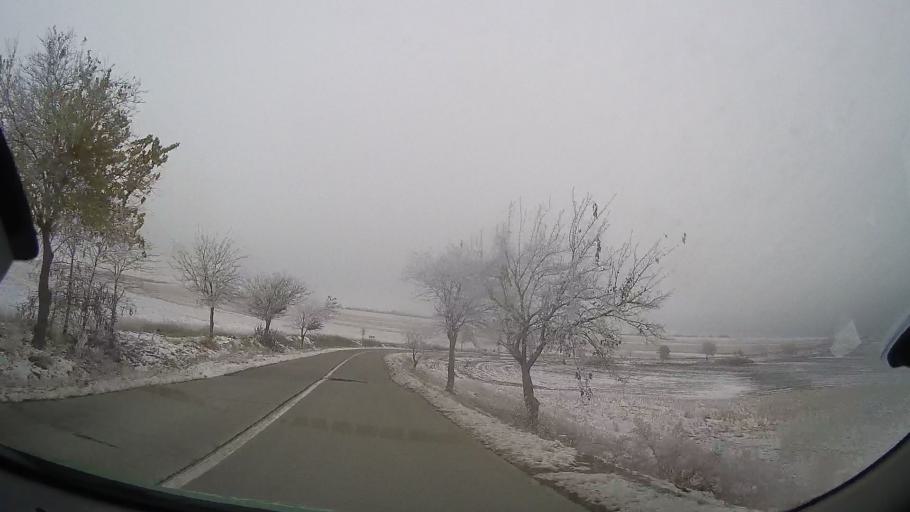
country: RO
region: Vaslui
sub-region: Comuna Ivesti
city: Ivesti
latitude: 46.1967
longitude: 27.5909
